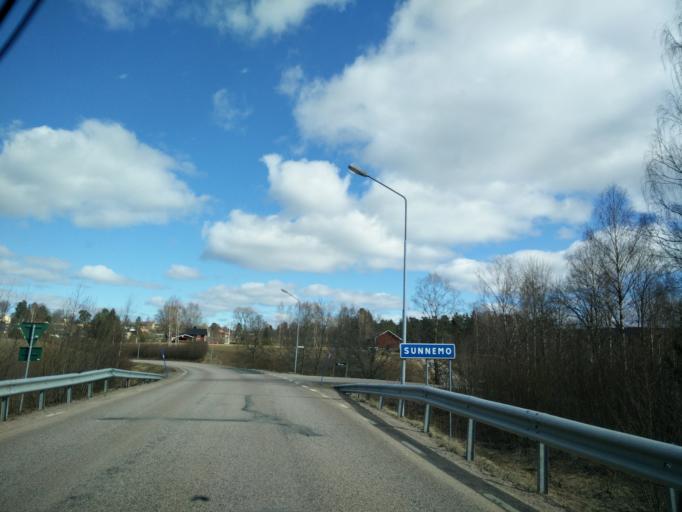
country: SE
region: Vaermland
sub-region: Hagfors Kommun
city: Hagfors
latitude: 59.8805
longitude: 13.7105
